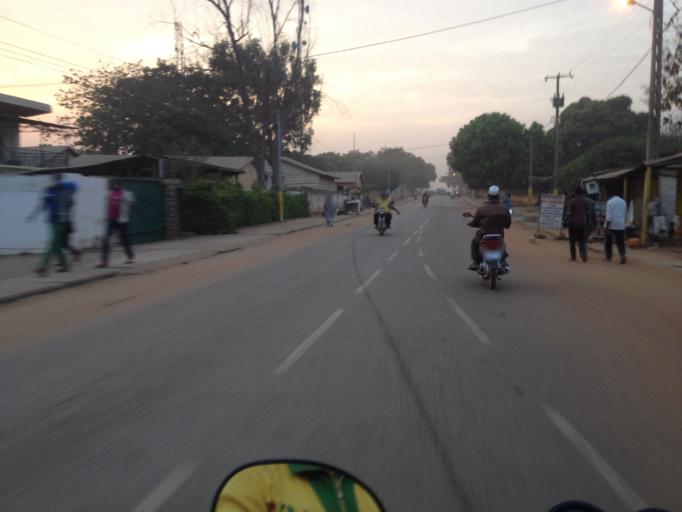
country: BJ
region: Borgou
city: Parakou
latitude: 9.3398
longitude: 2.6319
